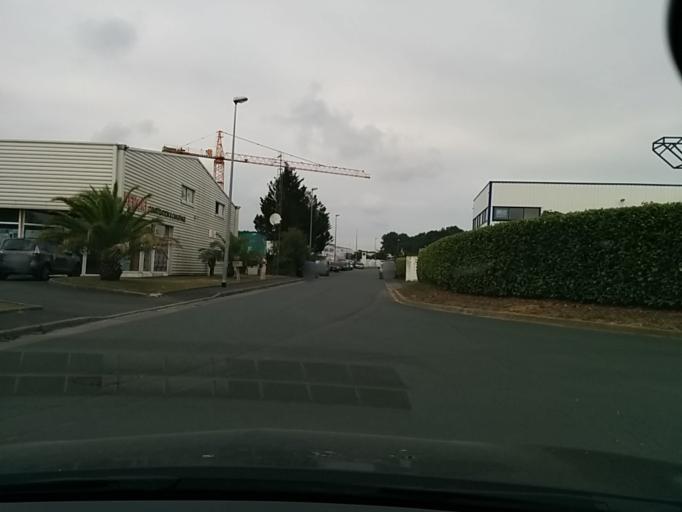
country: FR
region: Aquitaine
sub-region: Departement des Pyrenees-Atlantiques
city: Anglet
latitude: 43.4637
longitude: -1.5014
